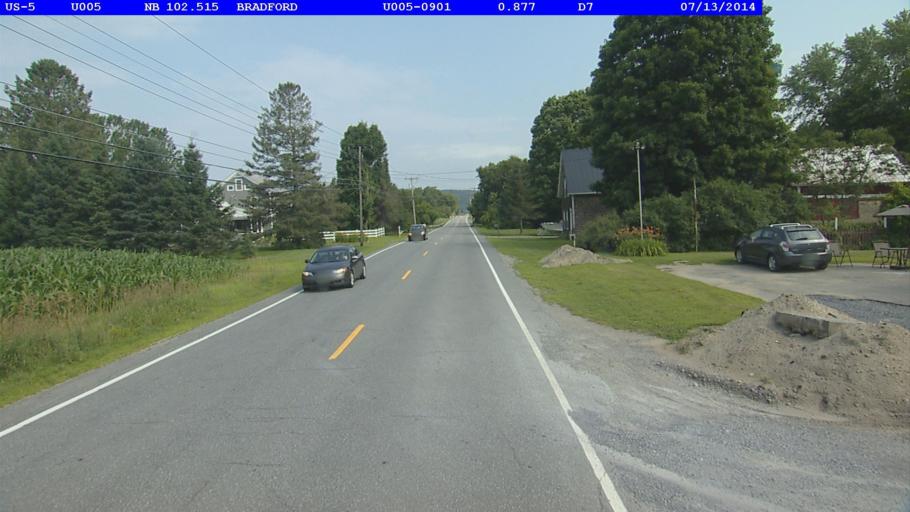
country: US
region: New Hampshire
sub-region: Grafton County
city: Orford
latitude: 43.9742
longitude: -72.1173
